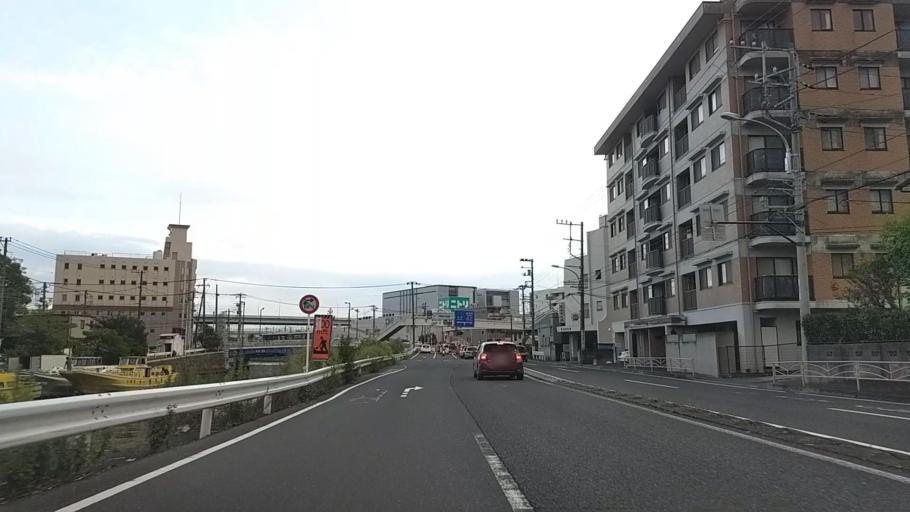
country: JP
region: Kanagawa
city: Yokohama
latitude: 35.4162
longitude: 139.6269
